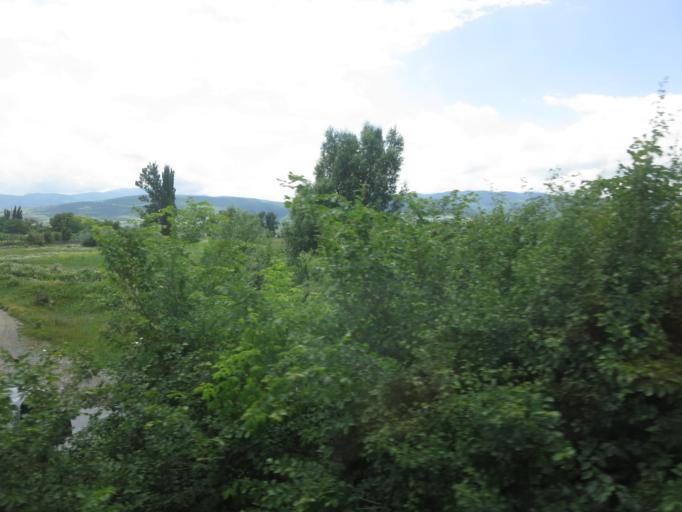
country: GE
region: Shida Kartli
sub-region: Khashuris Raioni
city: Khashuri
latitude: 42.0113
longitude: 43.6865
